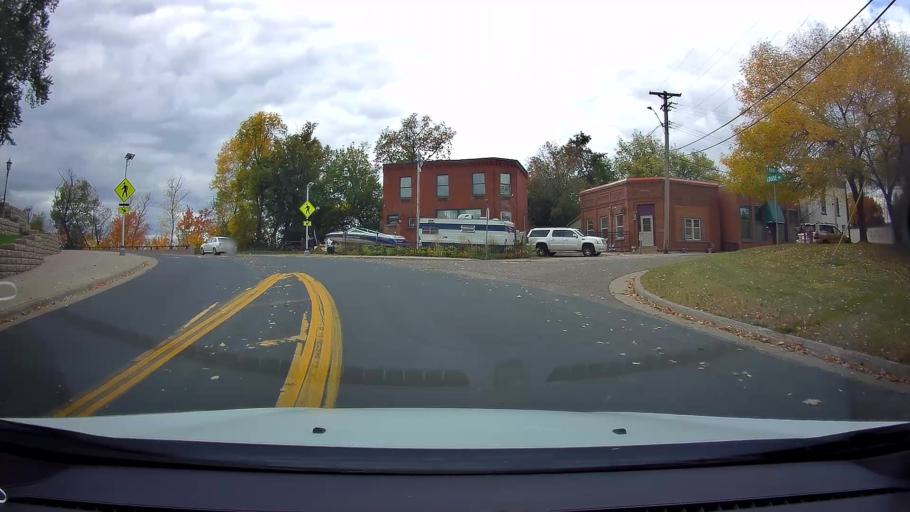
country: US
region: Minnesota
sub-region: Chisago County
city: Center City
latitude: 45.3969
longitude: -92.8184
